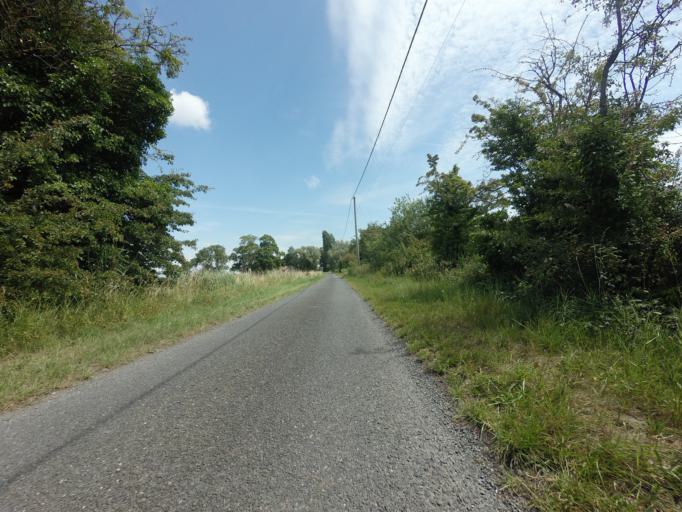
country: GB
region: England
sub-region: Kent
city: Stone
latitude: 51.0010
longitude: 0.8239
